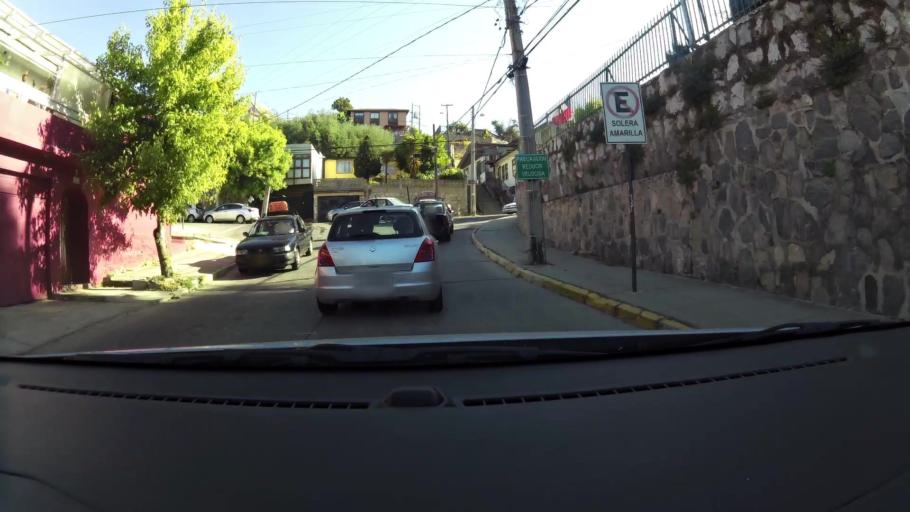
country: CL
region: Valparaiso
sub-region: Provincia de Valparaiso
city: Vina del Mar
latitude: -33.0319
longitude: -71.5632
